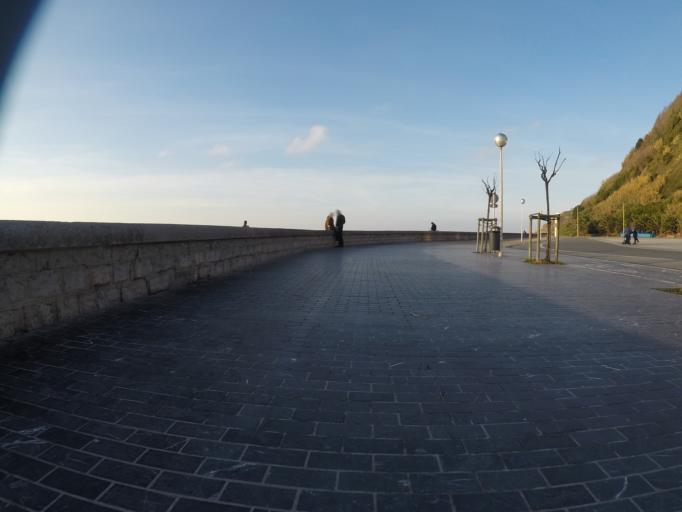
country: ES
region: Basque Country
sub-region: Provincia de Guipuzcoa
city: San Sebastian
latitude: 43.3283
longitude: -1.9717
